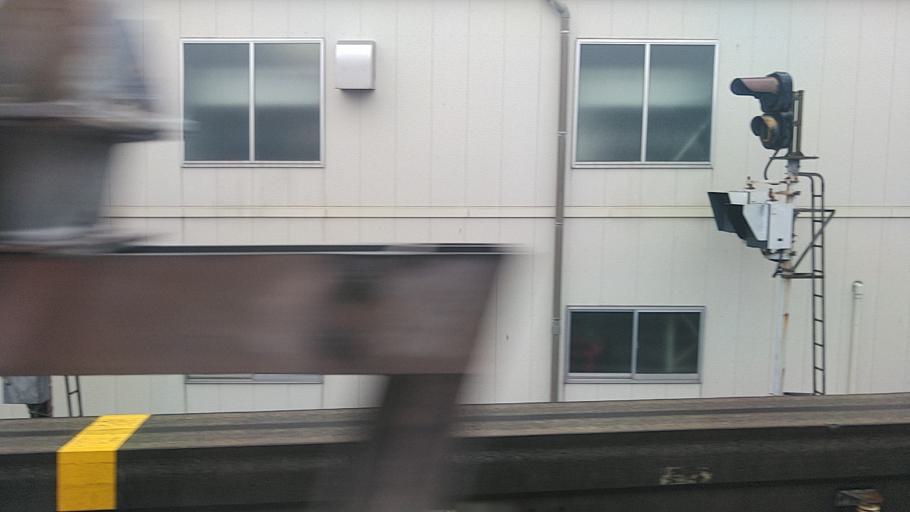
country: JP
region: Kanagawa
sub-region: Kawasaki-shi
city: Kawasaki
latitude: 35.5707
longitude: 139.7498
